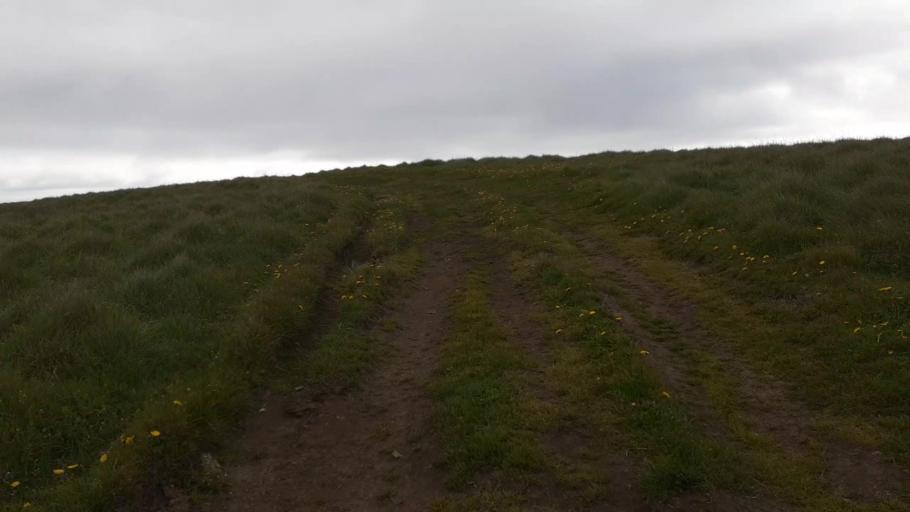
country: IS
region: Northeast
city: Dalvik
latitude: 66.5418
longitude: -17.9847
